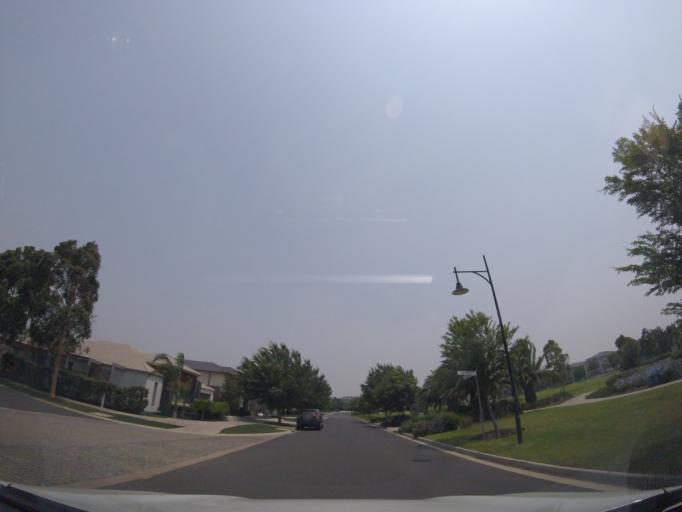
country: AU
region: Victoria
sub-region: Hume
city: Greenvale
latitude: -37.6237
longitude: 144.8887
